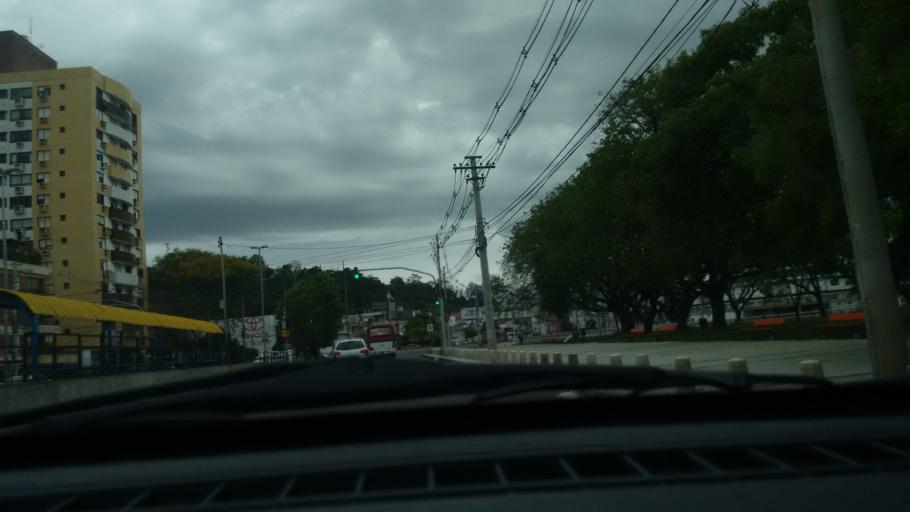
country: BR
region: Rio Grande do Sul
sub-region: Porto Alegre
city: Porto Alegre
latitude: -30.0627
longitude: -51.2316
